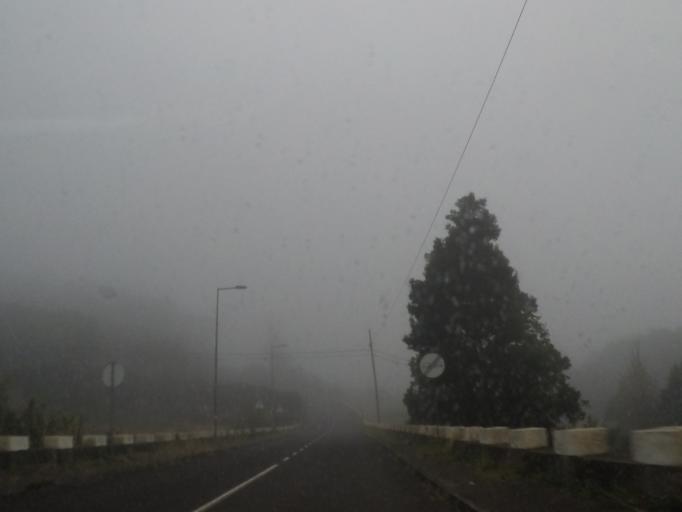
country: PT
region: Madeira
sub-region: Santa Cruz
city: Camacha
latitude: 32.7257
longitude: -16.8271
